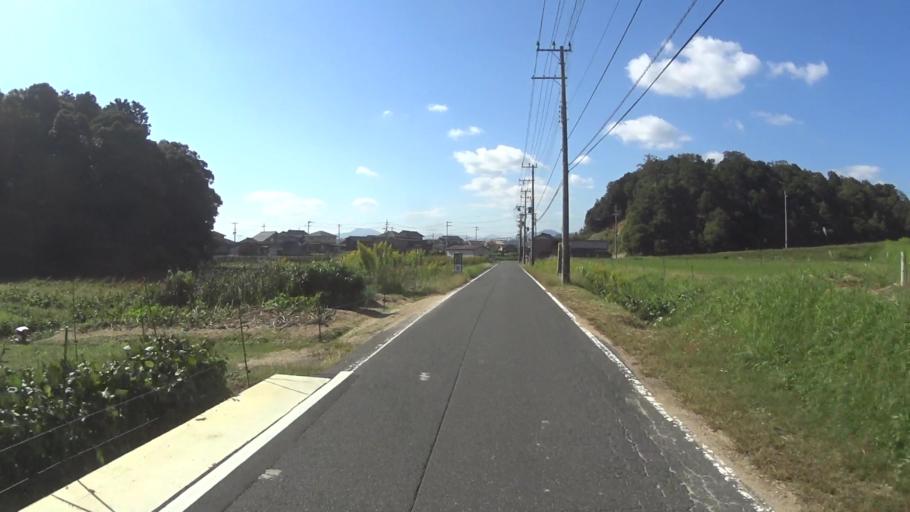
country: JP
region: Kyoto
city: Miyazu
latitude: 35.6843
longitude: 135.0930
